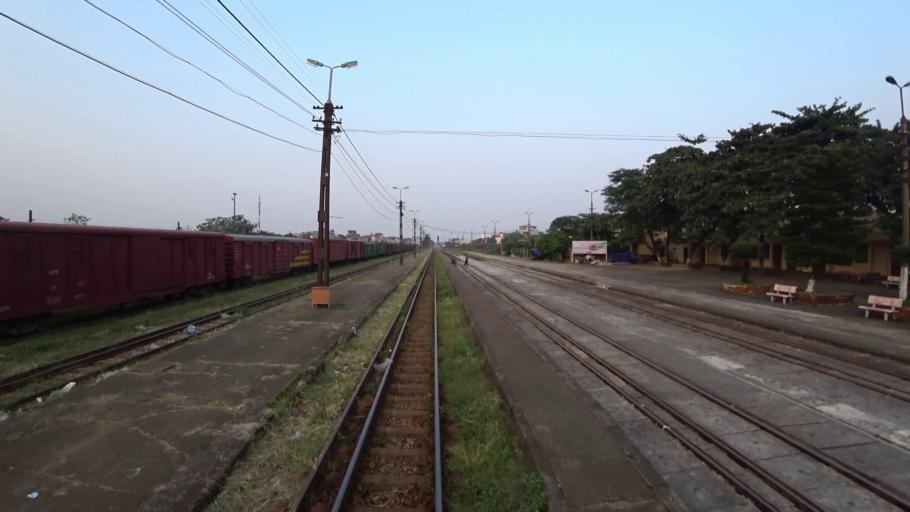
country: VN
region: Ha Noi
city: Dong Anh
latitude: 21.0981
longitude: 105.9088
